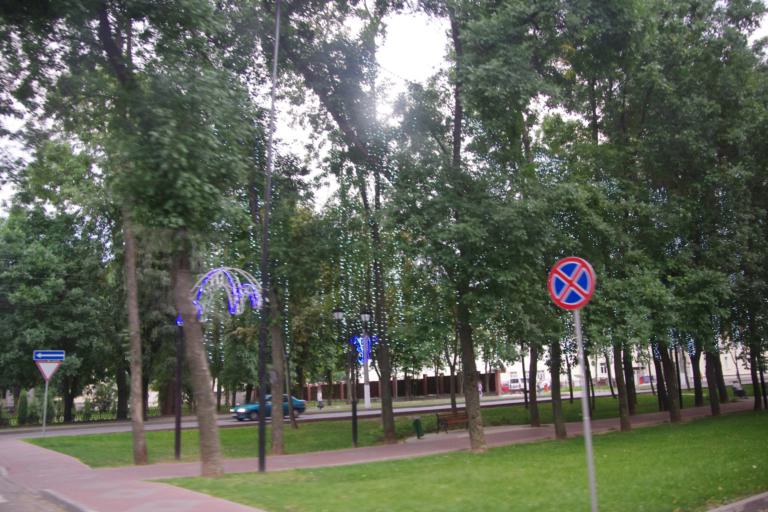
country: BY
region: Vitebsk
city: Vitebsk
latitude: 55.1858
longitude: 30.2067
